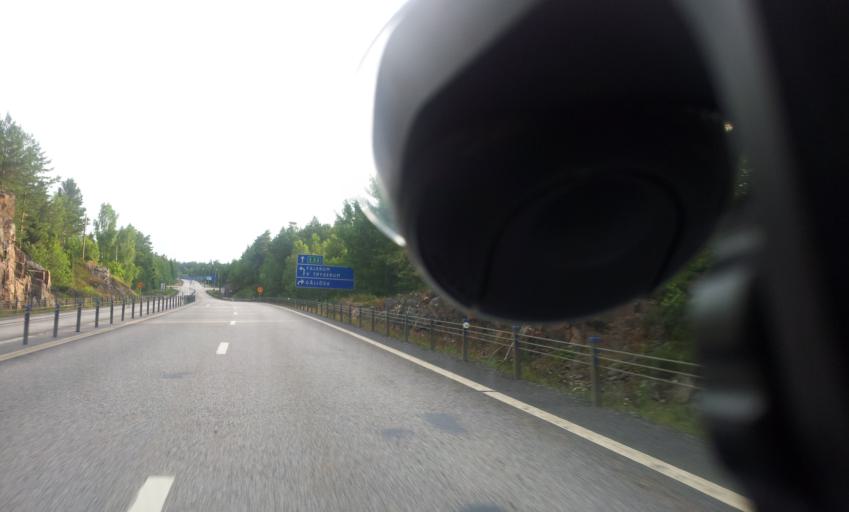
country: SE
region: OEstergoetland
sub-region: Valdemarsviks Kommun
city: Valdemarsvik
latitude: 58.1549
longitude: 16.5439
